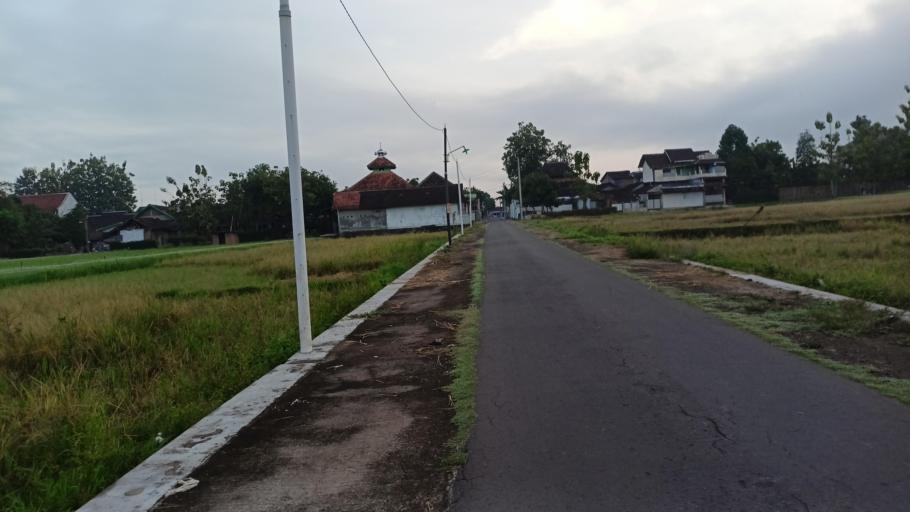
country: ID
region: Central Java
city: Jaten
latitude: -7.5922
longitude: 110.9158
